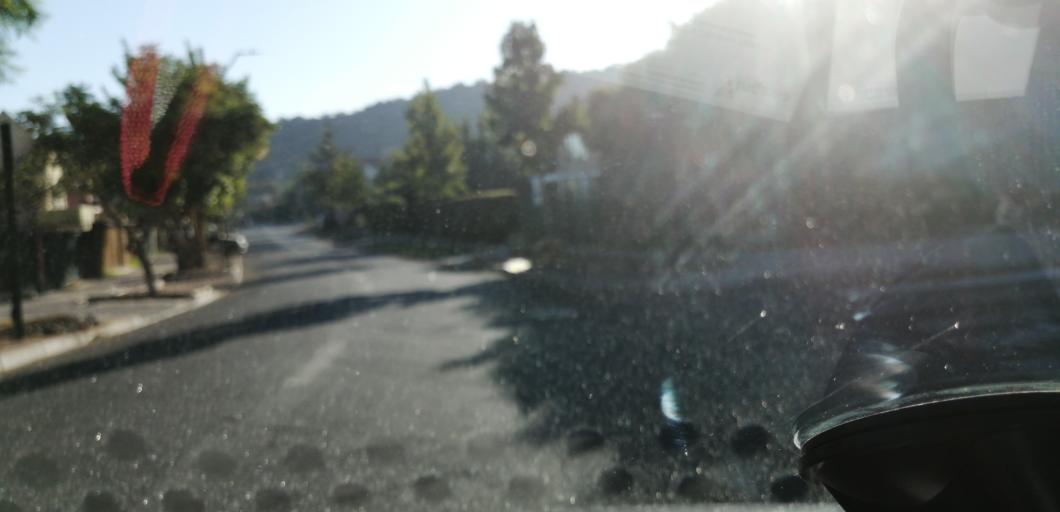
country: CL
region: Santiago Metropolitan
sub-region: Provincia de Santiago
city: Lo Prado
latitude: -33.4511
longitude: -70.8392
